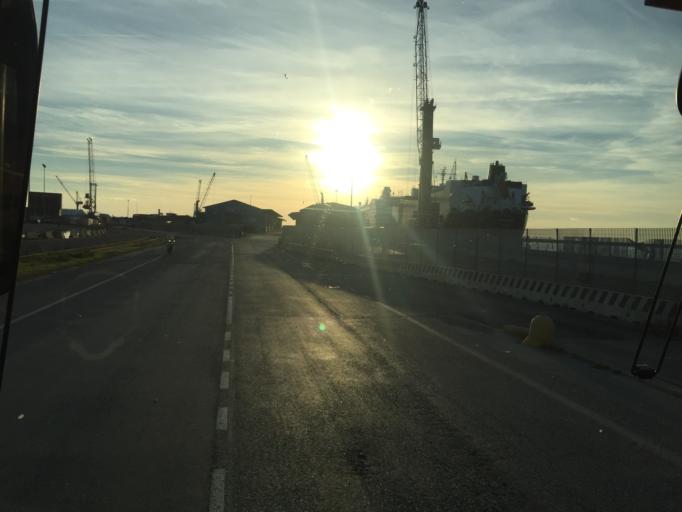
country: IT
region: Tuscany
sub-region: Provincia di Livorno
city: Livorno
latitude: 43.5569
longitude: 10.3012
